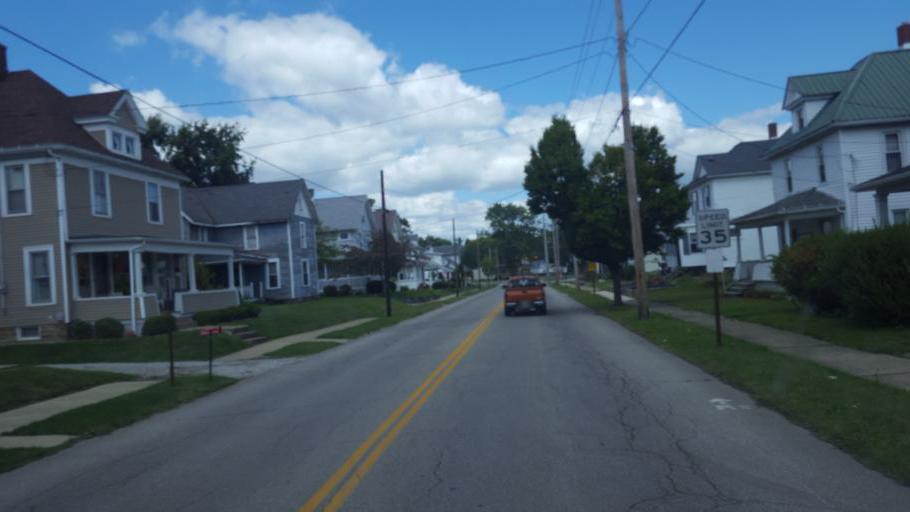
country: US
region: Ohio
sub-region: Ashland County
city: Ashland
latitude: 40.8769
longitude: -82.3128
